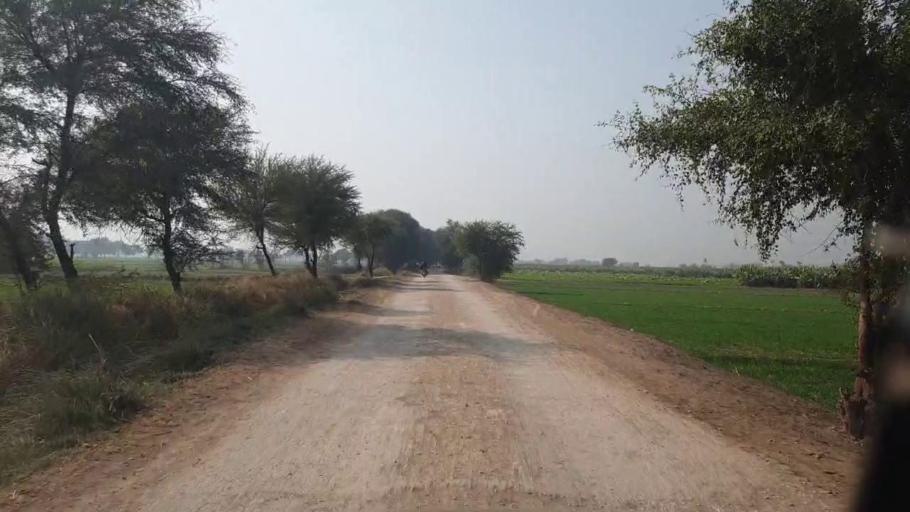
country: PK
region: Sindh
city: Shahdadpur
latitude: 26.0165
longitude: 68.5289
